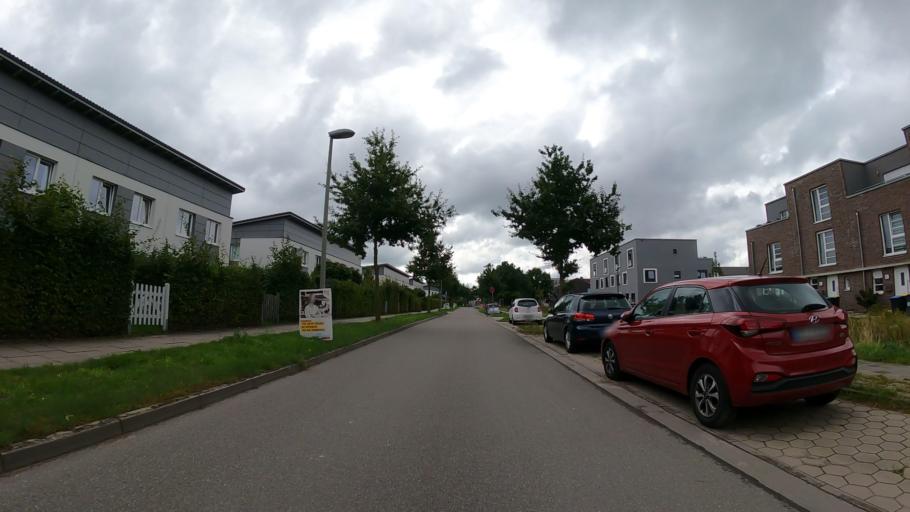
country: DE
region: Lower Saxony
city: Neu Wulmstorf
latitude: 53.4781
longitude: 9.8533
